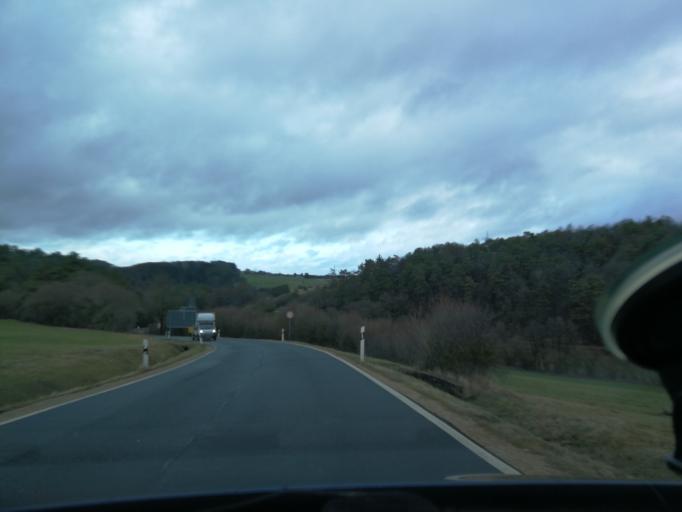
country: DE
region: Rheinland-Pfalz
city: Nohn
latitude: 50.3144
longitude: 6.7746
